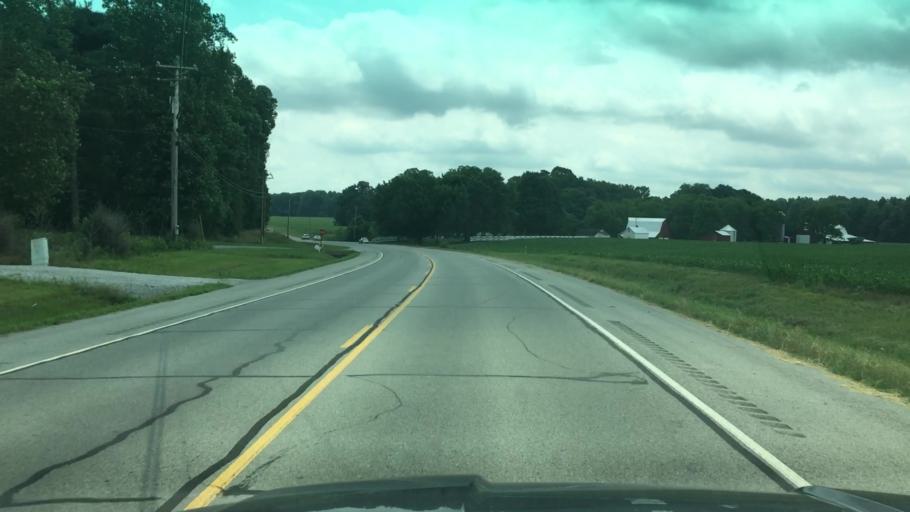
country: US
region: Tennessee
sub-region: Coffee County
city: New Union
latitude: 35.5268
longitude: -86.1573
